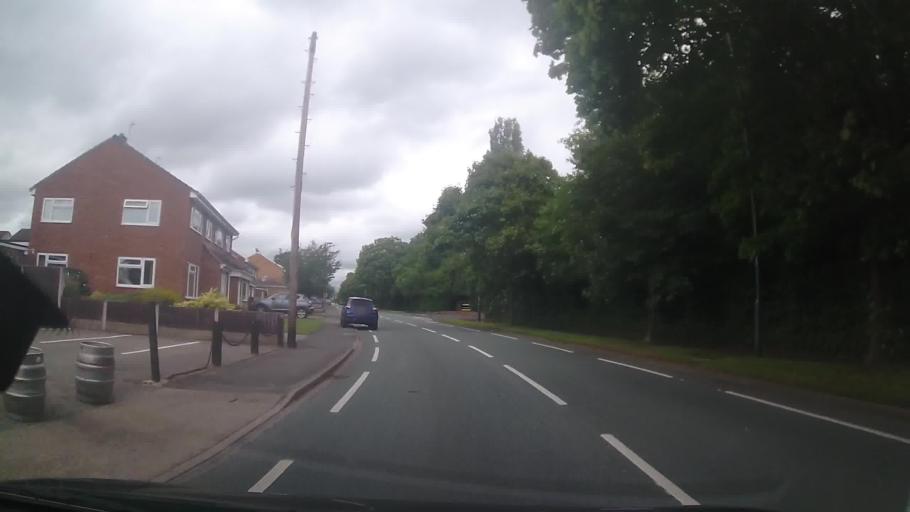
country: GB
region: England
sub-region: Shropshire
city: Shrewsbury
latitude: 52.7301
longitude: -2.7421
